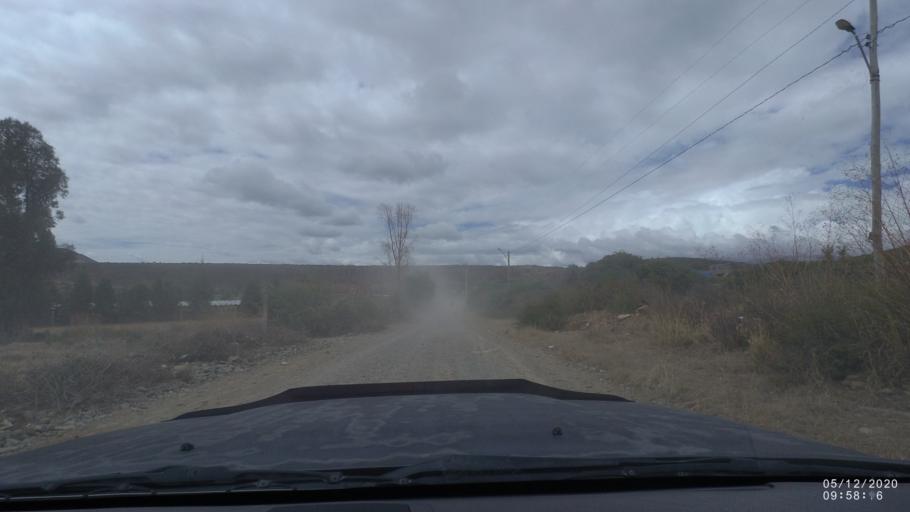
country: BO
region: Cochabamba
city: Sipe Sipe
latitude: -17.4285
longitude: -66.2912
